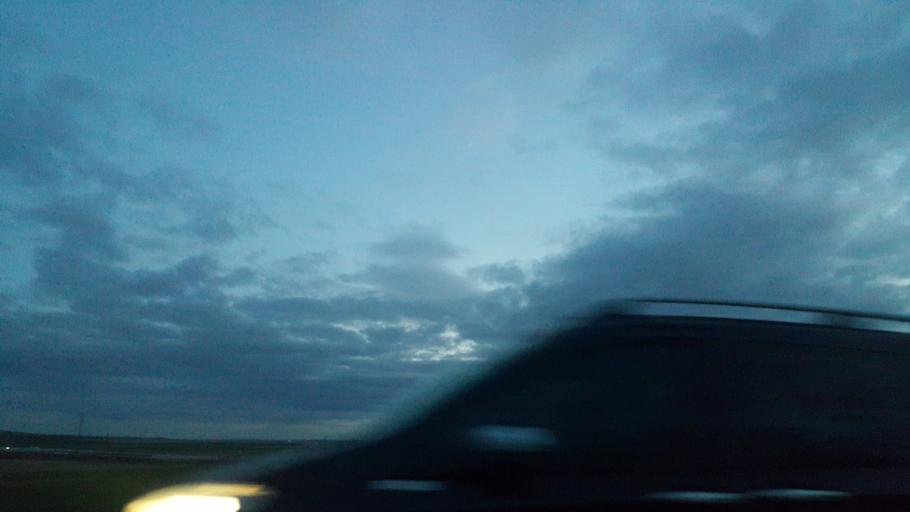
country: TR
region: Konya
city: Kulu
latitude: 39.1670
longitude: 33.1708
